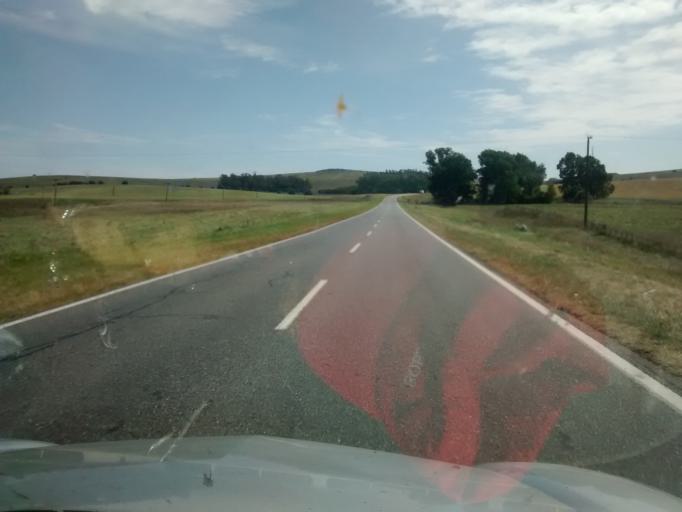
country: AR
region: Buenos Aires
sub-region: Partido de Balcarce
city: Balcarce
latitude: -37.6420
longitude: -58.5987
